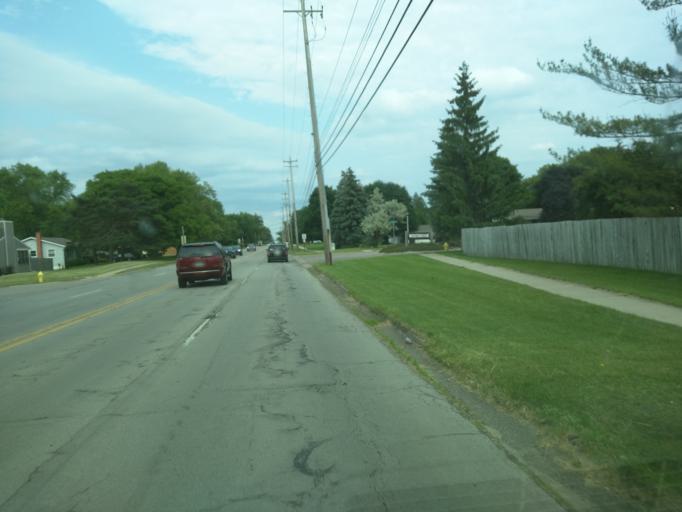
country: US
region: Michigan
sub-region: Eaton County
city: Waverly
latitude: 42.7265
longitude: -84.6194
